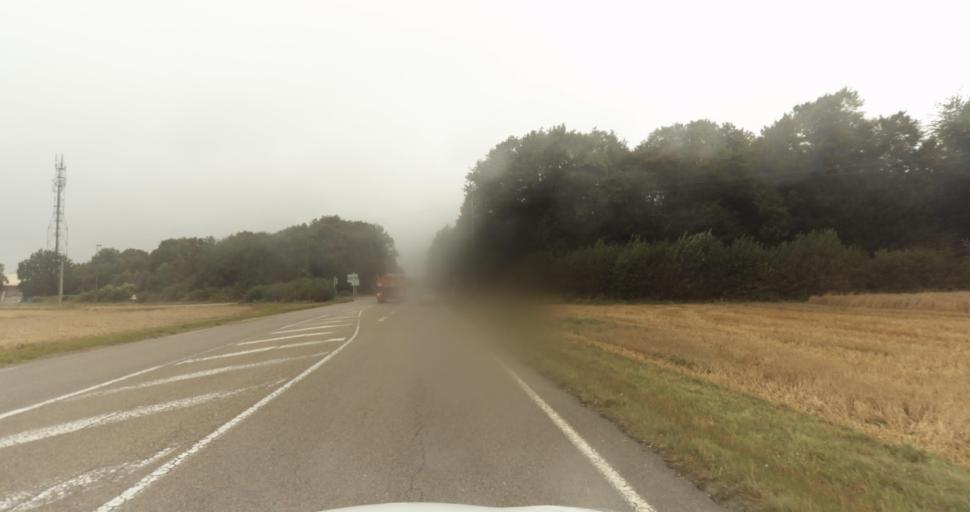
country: FR
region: Haute-Normandie
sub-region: Departement de l'Eure
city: Normanville
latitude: 49.0908
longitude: 1.1771
